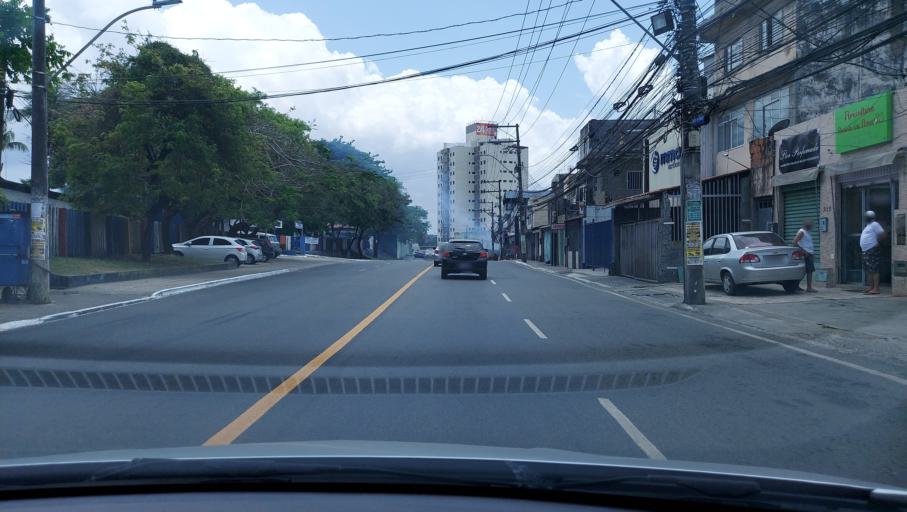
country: BR
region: Bahia
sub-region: Salvador
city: Salvador
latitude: -12.9591
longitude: -38.4674
